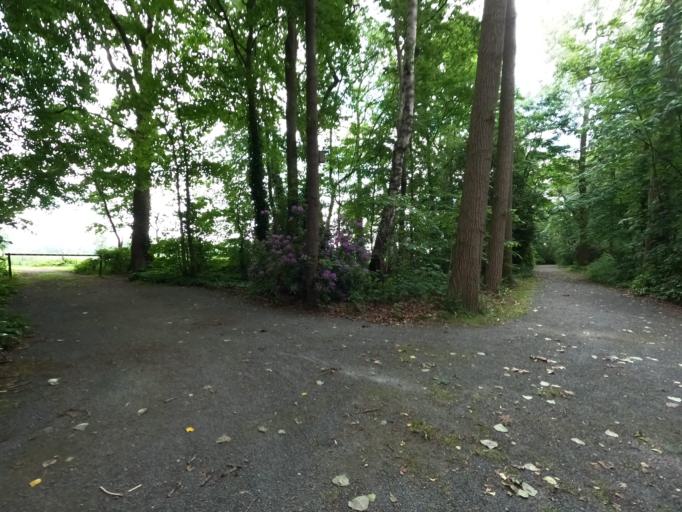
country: BE
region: Flanders
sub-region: Provincie Antwerpen
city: Kalmthout
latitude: 51.3968
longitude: 4.4817
